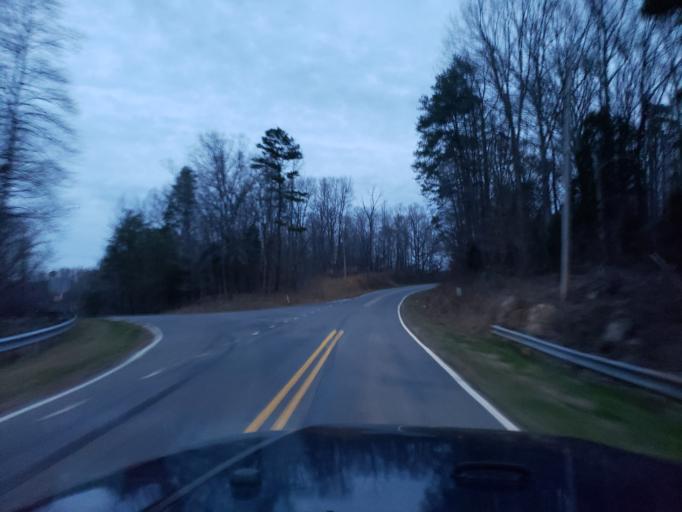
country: US
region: North Carolina
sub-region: Cleveland County
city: White Plains
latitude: 35.1717
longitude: -81.4008
